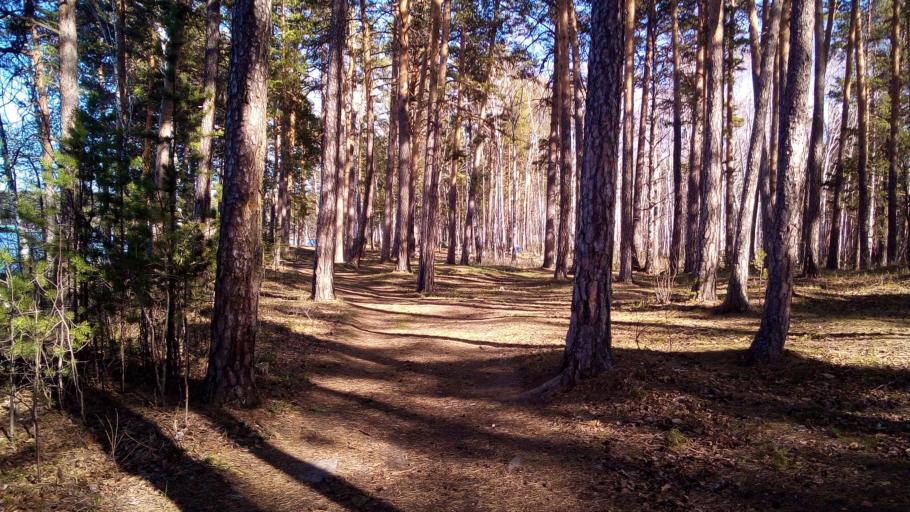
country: RU
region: Chelyabinsk
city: Chebarkul'
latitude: 55.1137
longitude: 60.3338
